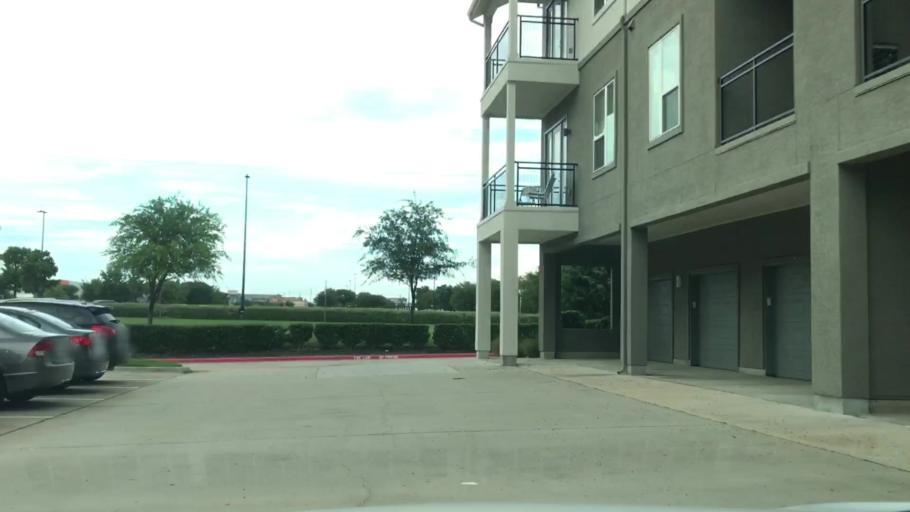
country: US
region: Texas
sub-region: Collin County
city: Frisco
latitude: 33.0938
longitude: -96.7982
